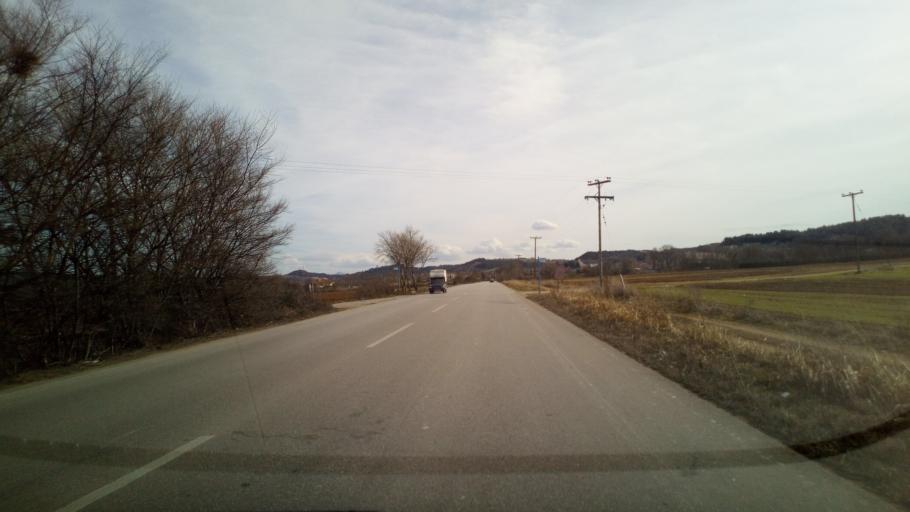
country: GR
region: Central Macedonia
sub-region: Nomos Thessalonikis
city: Gerakarou
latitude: 40.6417
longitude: 23.1832
